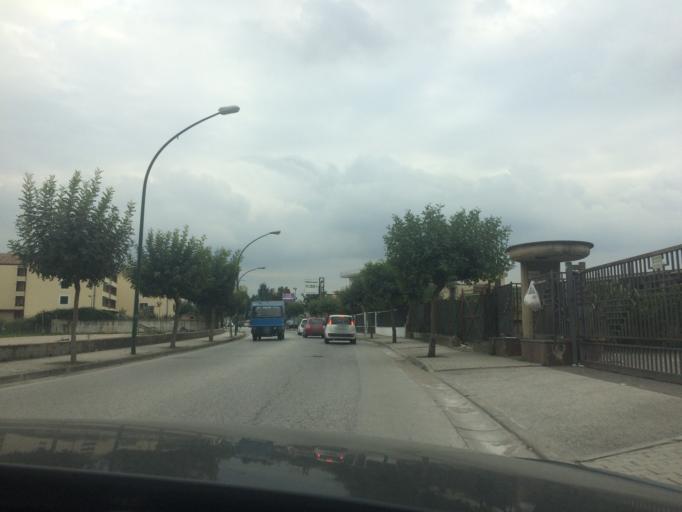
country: IT
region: Campania
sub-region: Provincia di Napoli
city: Palma Campania
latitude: 40.8706
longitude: 14.5471
